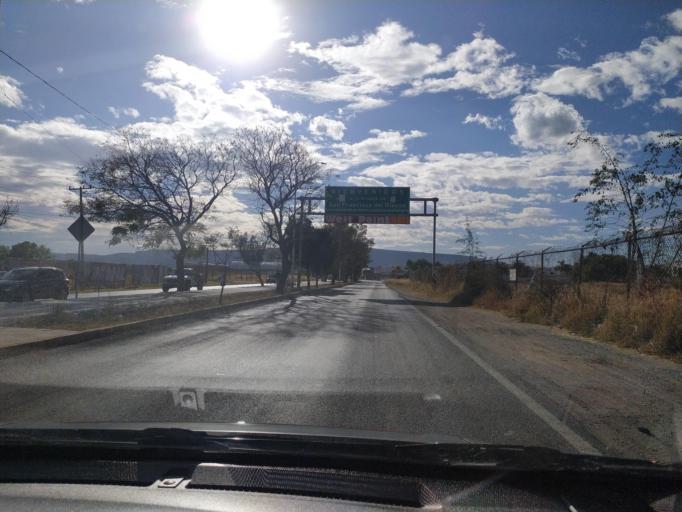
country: LA
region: Oudomxai
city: Muang La
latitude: 21.0322
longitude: 101.8392
